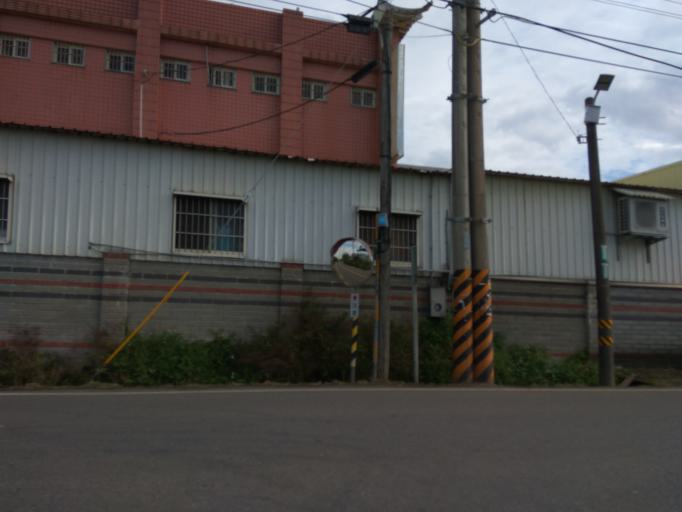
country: TW
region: Taiwan
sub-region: Hsinchu
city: Zhubei
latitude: 24.9563
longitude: 121.1105
